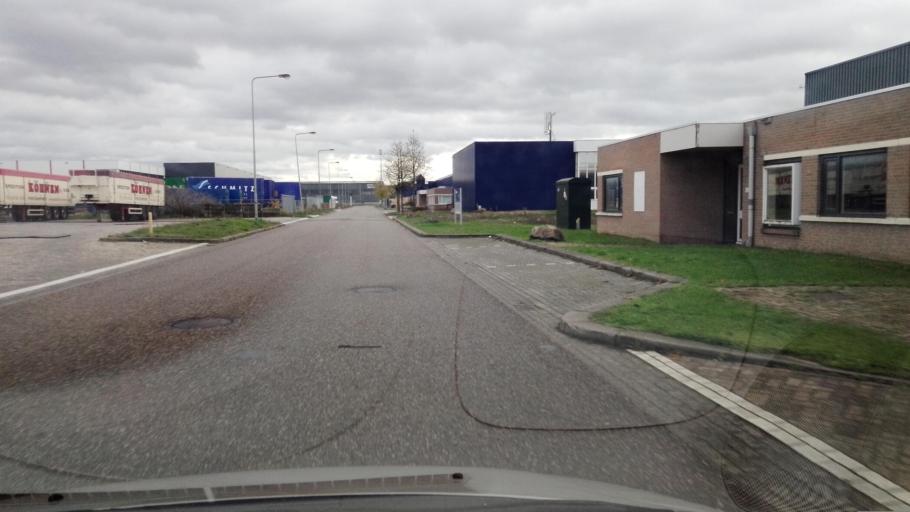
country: NL
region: Limburg
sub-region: Gemeente Roerdalen
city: Herkenbosch
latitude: 51.1680
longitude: 6.0474
